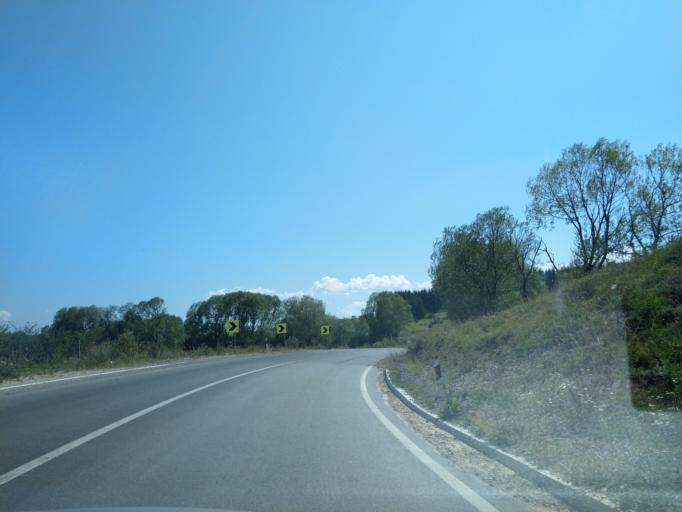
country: RS
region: Central Serbia
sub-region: Zlatiborski Okrug
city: Sjenica
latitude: 43.2814
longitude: 19.9683
